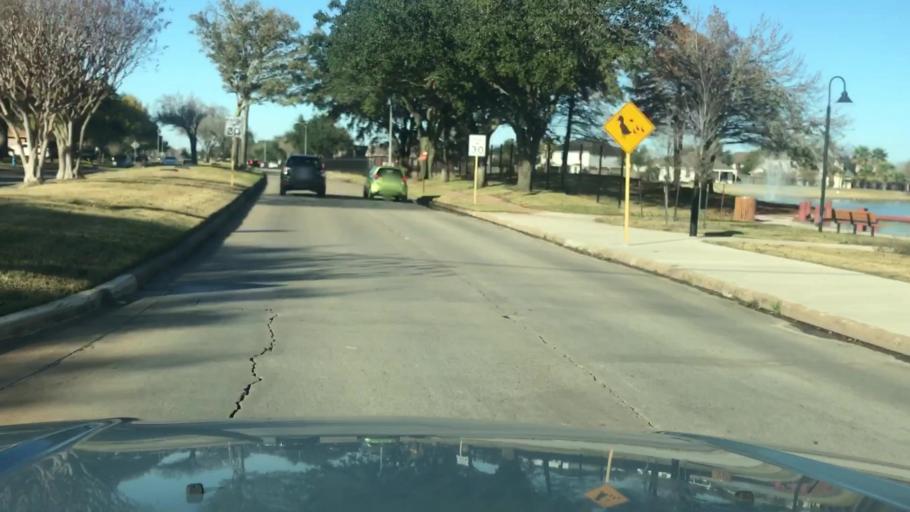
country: US
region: Texas
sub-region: Harris County
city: Katy
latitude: 29.8188
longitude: -95.7522
